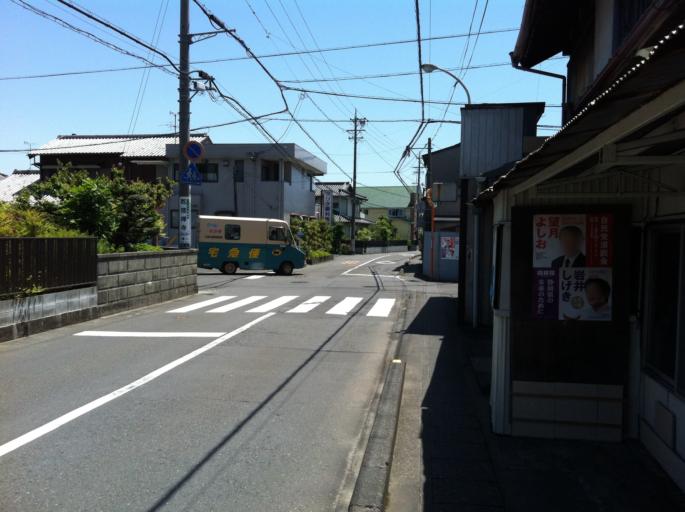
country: JP
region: Shizuoka
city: Shizuoka-shi
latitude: 35.0315
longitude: 138.4518
